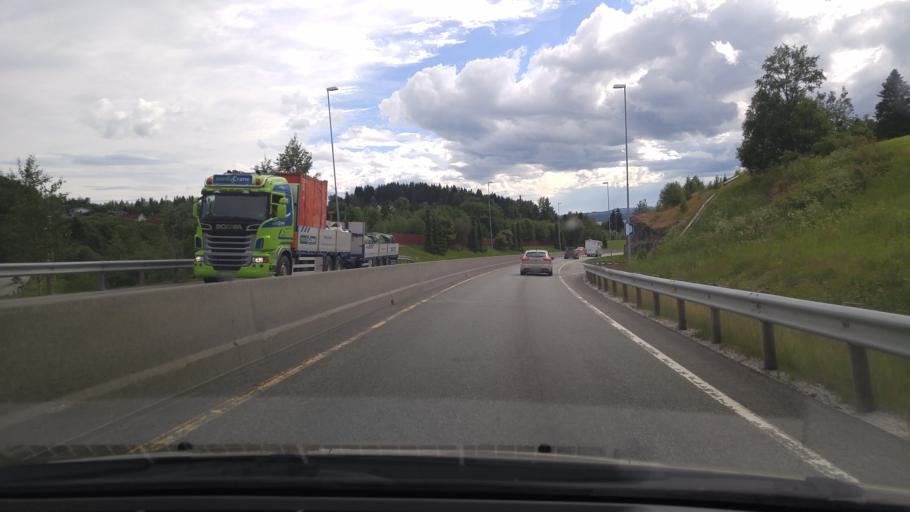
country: NO
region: Nord-Trondelag
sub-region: Steinkjer
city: Steinkjer
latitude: 64.0404
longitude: 11.4865
